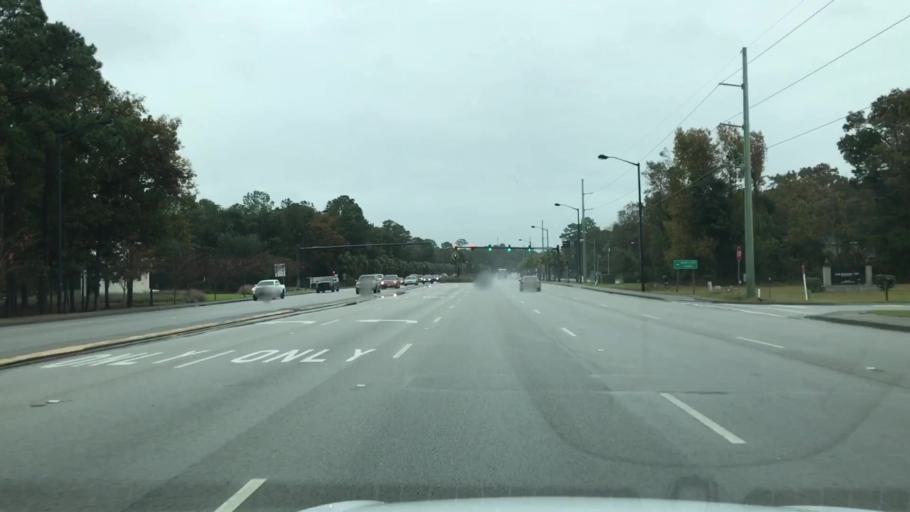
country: US
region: South Carolina
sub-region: Charleston County
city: Isle of Palms
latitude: 32.8801
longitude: -79.7622
